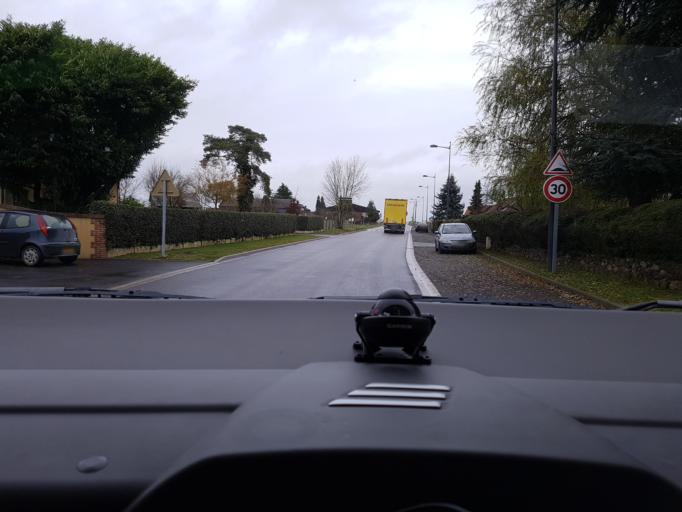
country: FR
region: Haute-Normandie
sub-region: Departement de l'Eure
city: Etrepagny
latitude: 49.3843
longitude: 1.5915
